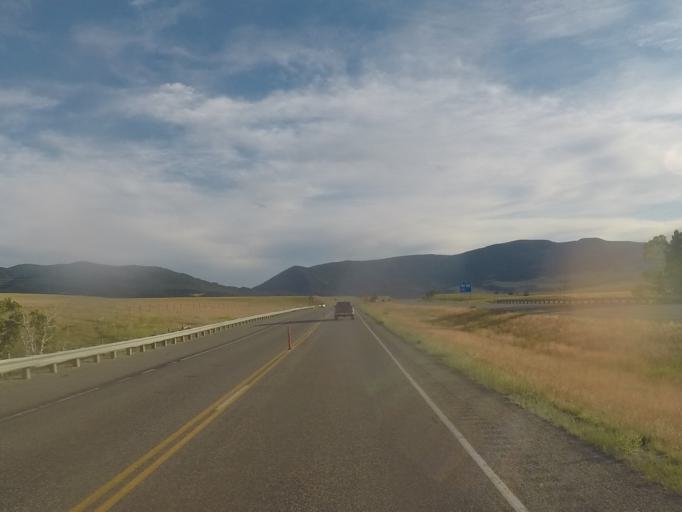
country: US
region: Montana
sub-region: Park County
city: Livingston
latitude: 45.6575
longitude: -110.5348
